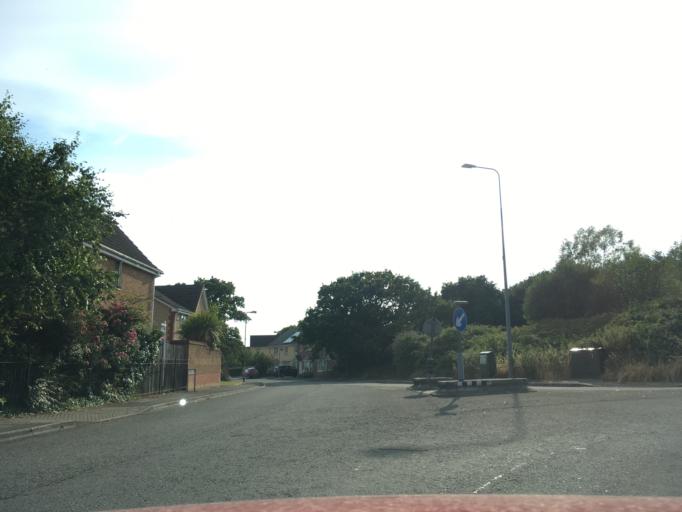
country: GB
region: Wales
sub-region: Newport
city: Marshfield
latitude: 51.5166
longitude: -3.0960
